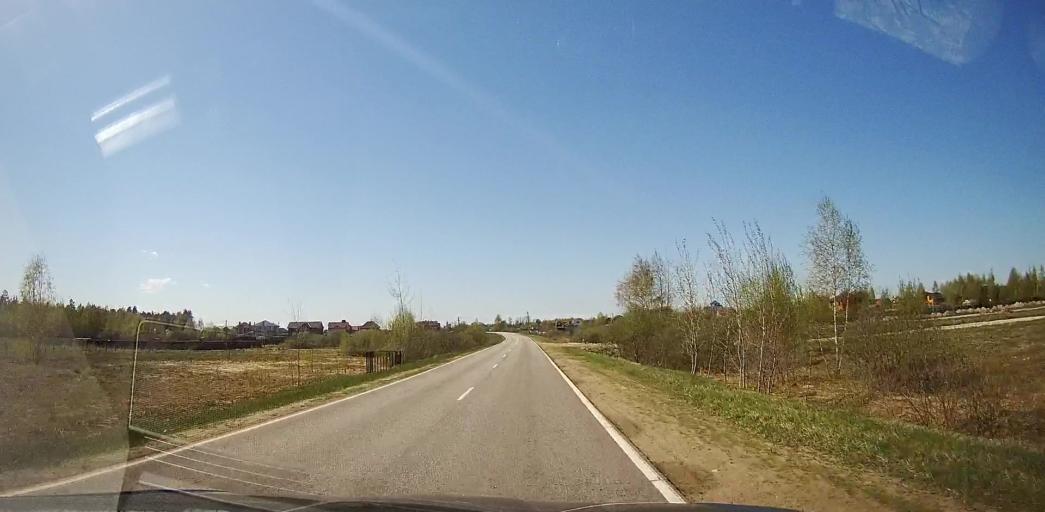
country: RU
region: Moskovskaya
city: Bronnitsy
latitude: 55.4564
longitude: 38.2881
